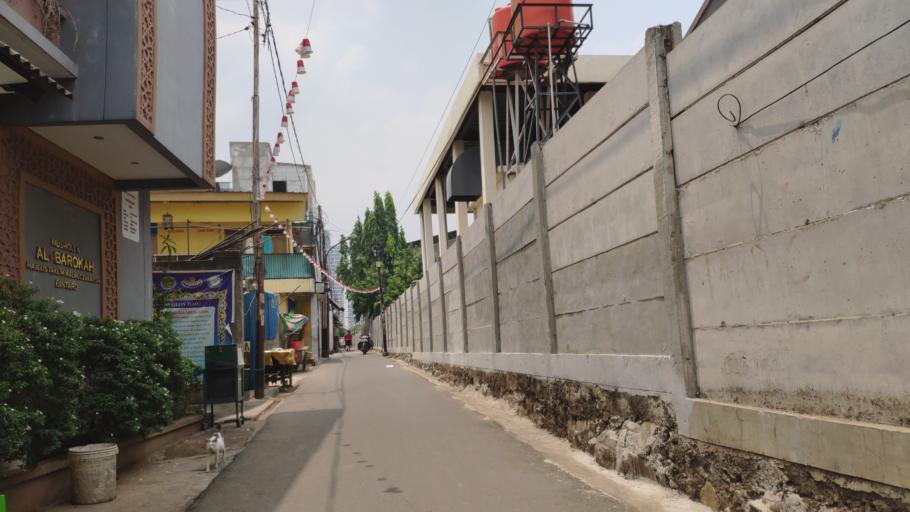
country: ID
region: Banten
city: South Tangerang
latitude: -6.2682
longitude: 106.7674
